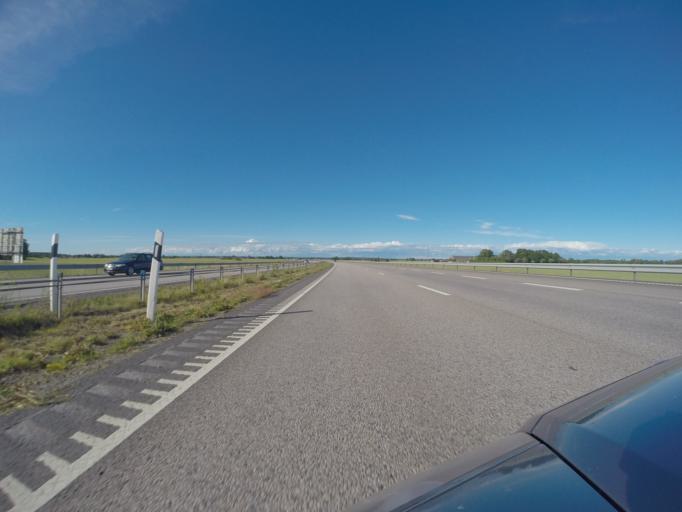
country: SE
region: Skane
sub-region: Helsingborg
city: Hyllinge
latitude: 56.1072
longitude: 12.8072
